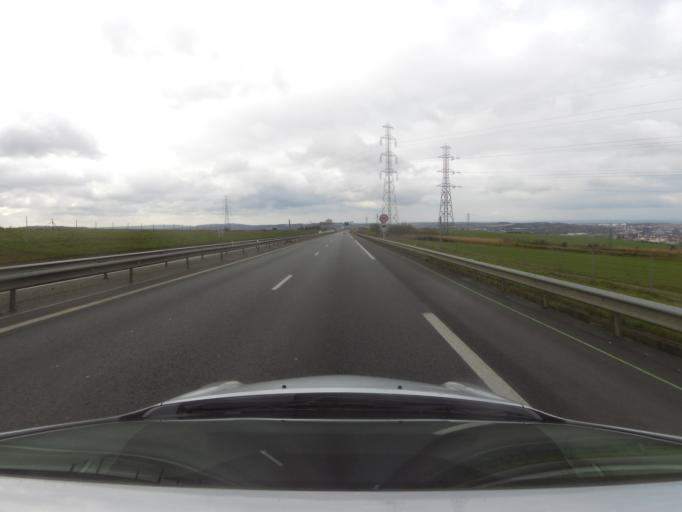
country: FR
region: Nord-Pas-de-Calais
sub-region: Departement du Pas-de-Calais
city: Boulogne-sur-Mer
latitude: 50.7135
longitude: 1.6438
